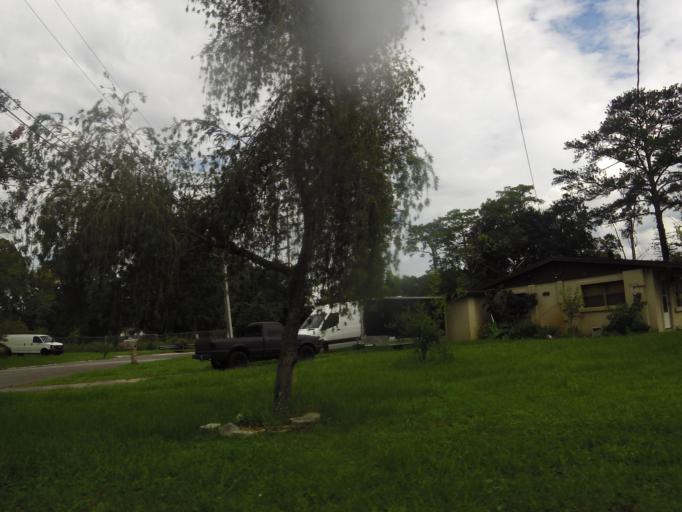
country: US
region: Florida
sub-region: Duval County
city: Jacksonville
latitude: 30.3124
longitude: -81.5362
